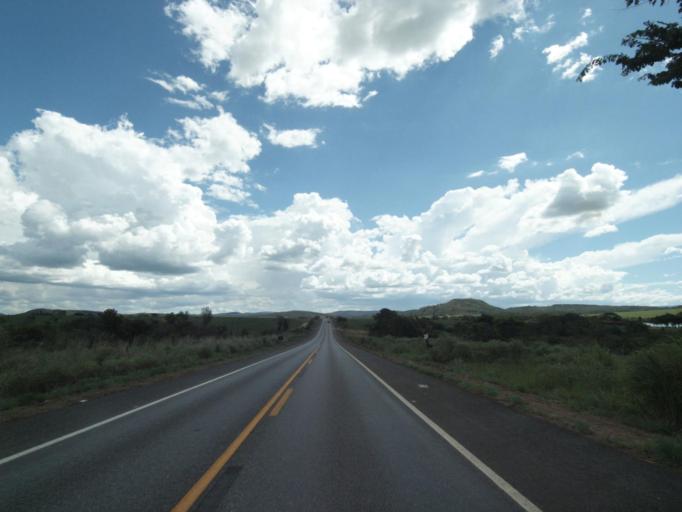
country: BR
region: Goias
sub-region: Pirenopolis
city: Pirenopolis
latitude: -15.5879
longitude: -48.6346
